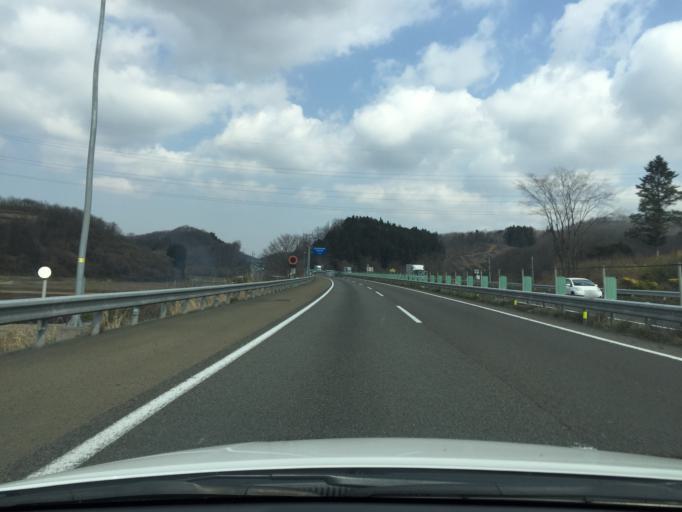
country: JP
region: Miyagi
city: Iwanuma
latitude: 38.1743
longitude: 140.7700
